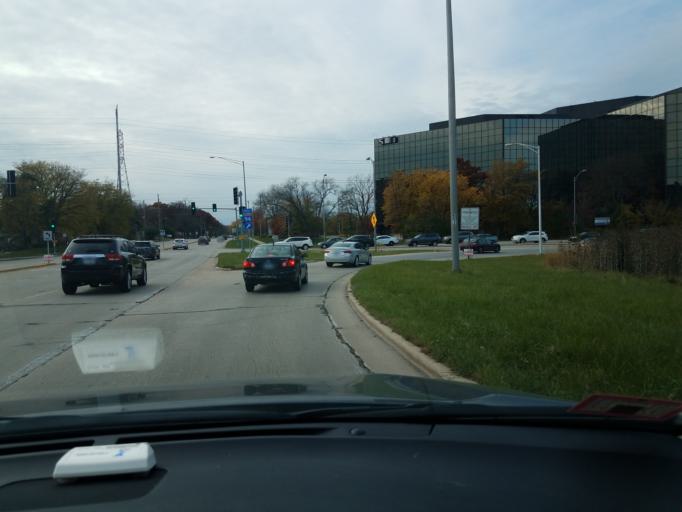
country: US
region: Illinois
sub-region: Cook County
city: Glenview
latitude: 42.0627
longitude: -87.7571
